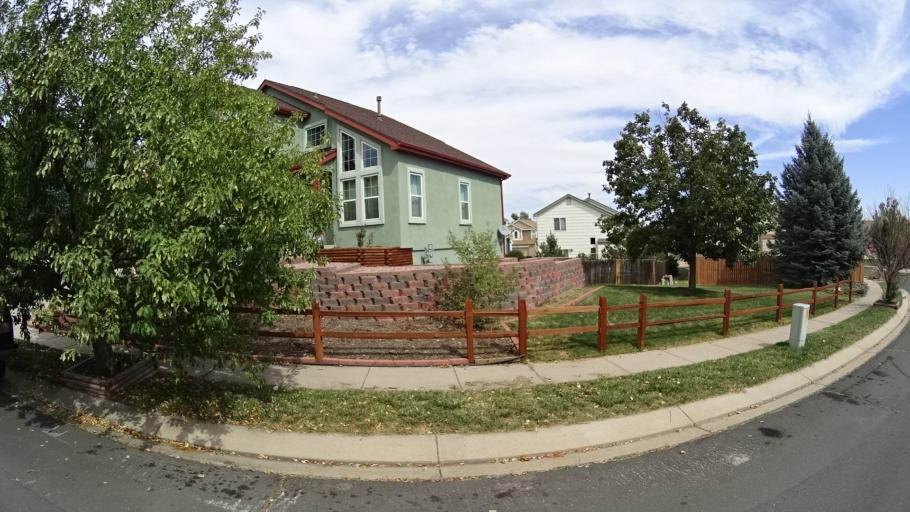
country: US
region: Colorado
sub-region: El Paso County
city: Cimarron Hills
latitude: 38.9020
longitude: -104.7164
